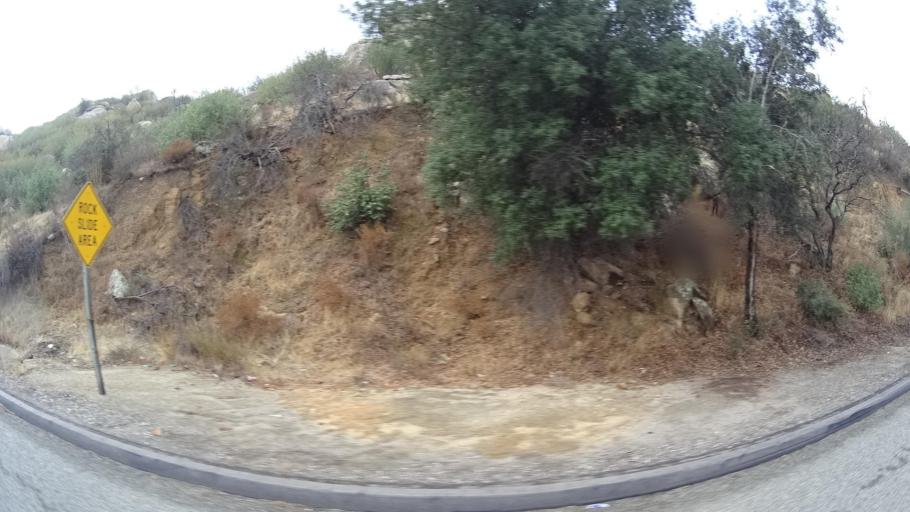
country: MX
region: Baja California
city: Tecate
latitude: 32.6012
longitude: -116.5973
